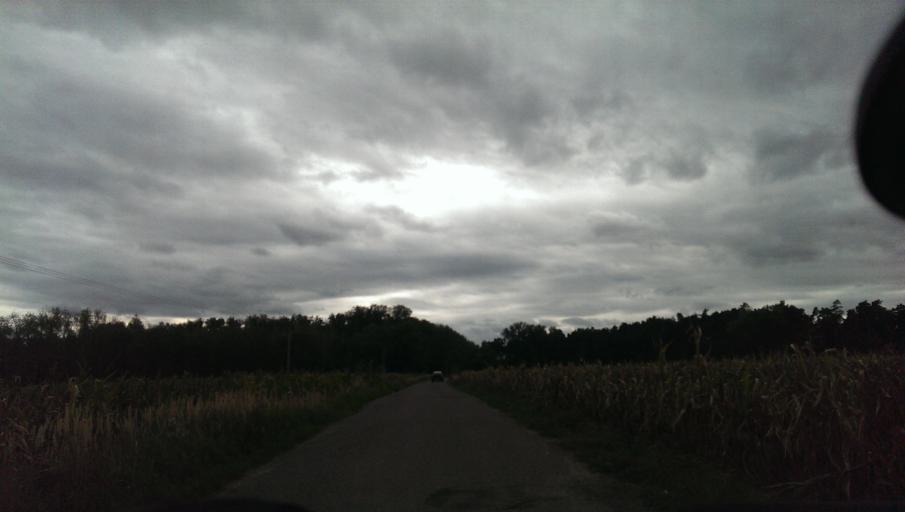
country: CZ
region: South Moravian
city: Moravsky Pisek
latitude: 48.9868
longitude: 17.3175
